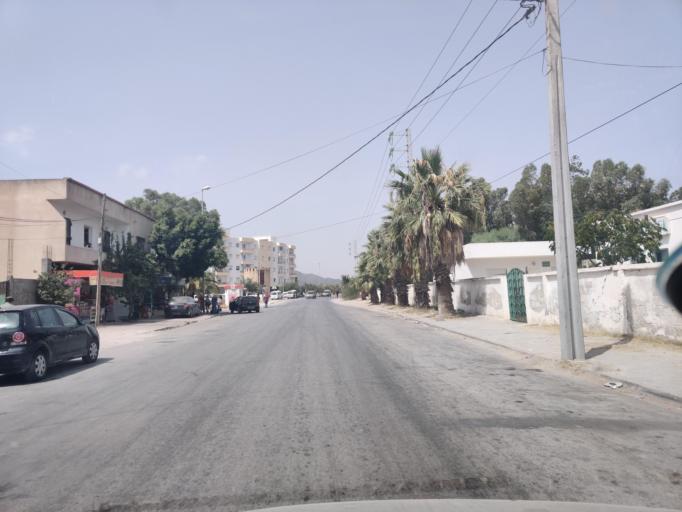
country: TN
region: Nabul
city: Bu `Urqub
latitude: 36.5993
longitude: 10.4935
